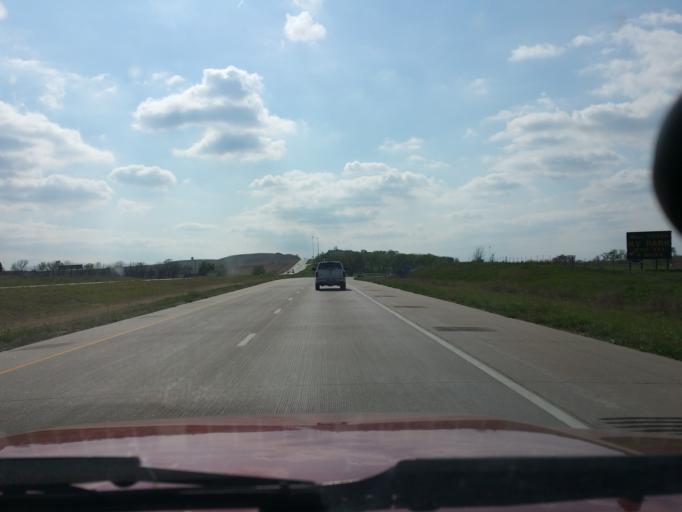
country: US
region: Kansas
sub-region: Pottawatomie County
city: Saint Marys
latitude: 39.0589
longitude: -96.1086
